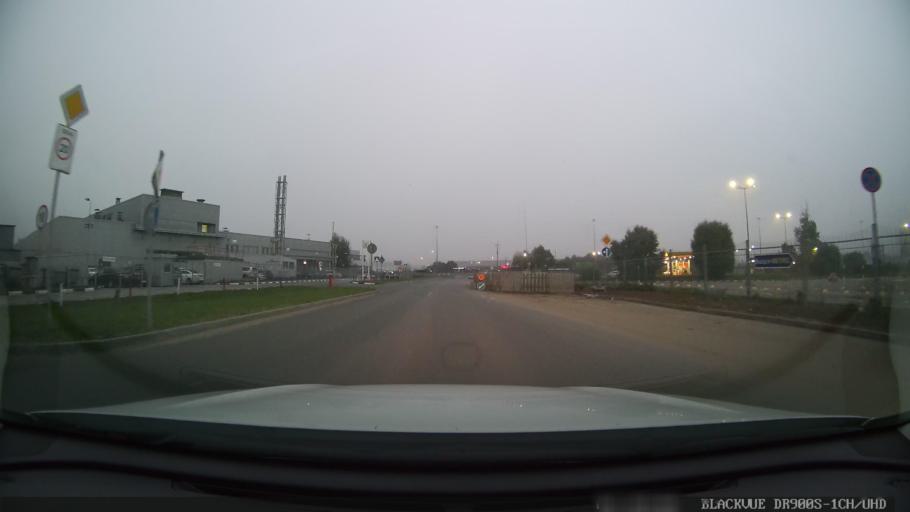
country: RU
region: Moscow
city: Solntsevo
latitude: 55.6193
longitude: 37.3902
